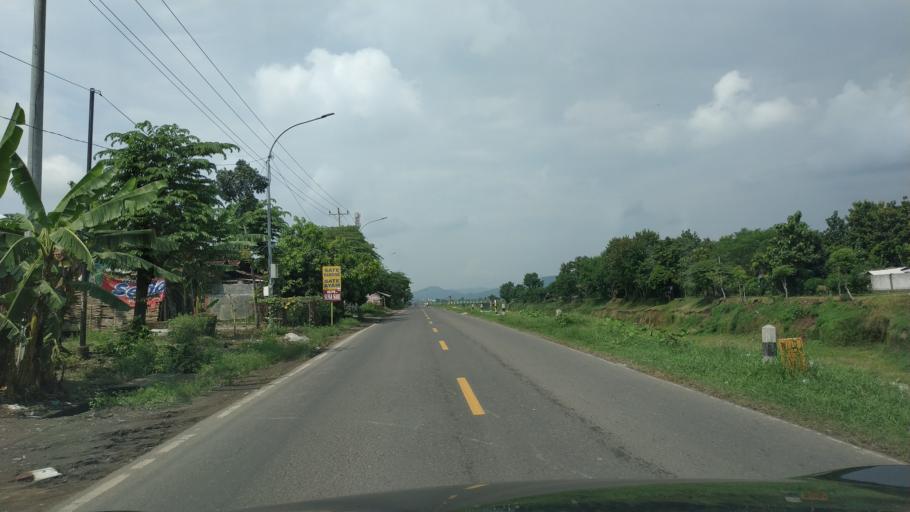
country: ID
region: Central Java
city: Margasari
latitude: -7.0724
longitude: 108.9831
